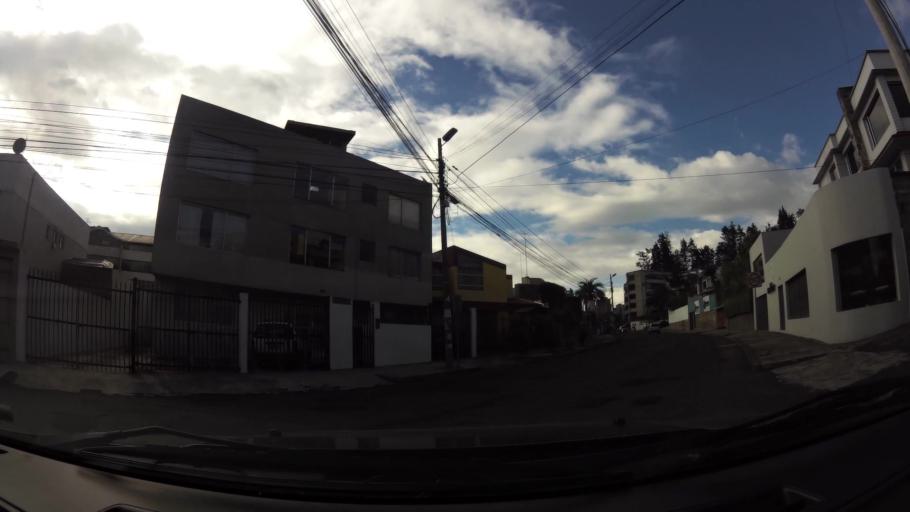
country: EC
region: Pichincha
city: Quito
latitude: -0.2056
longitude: -78.4813
